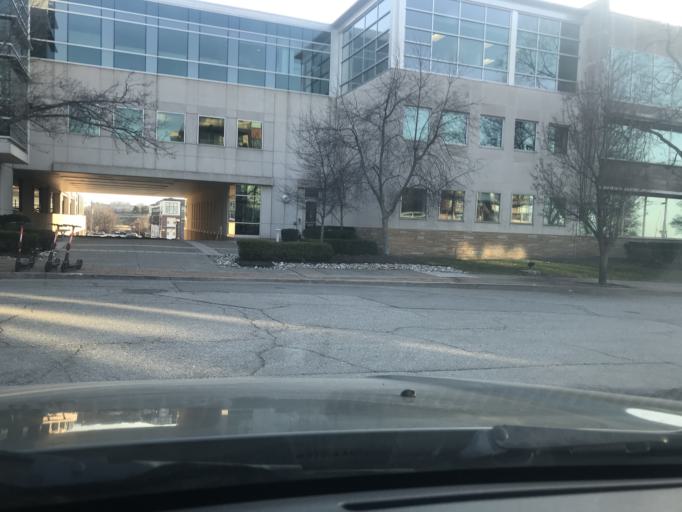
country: US
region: Missouri
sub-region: Jackson County
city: Kansas City
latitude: 39.1013
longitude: -94.5923
